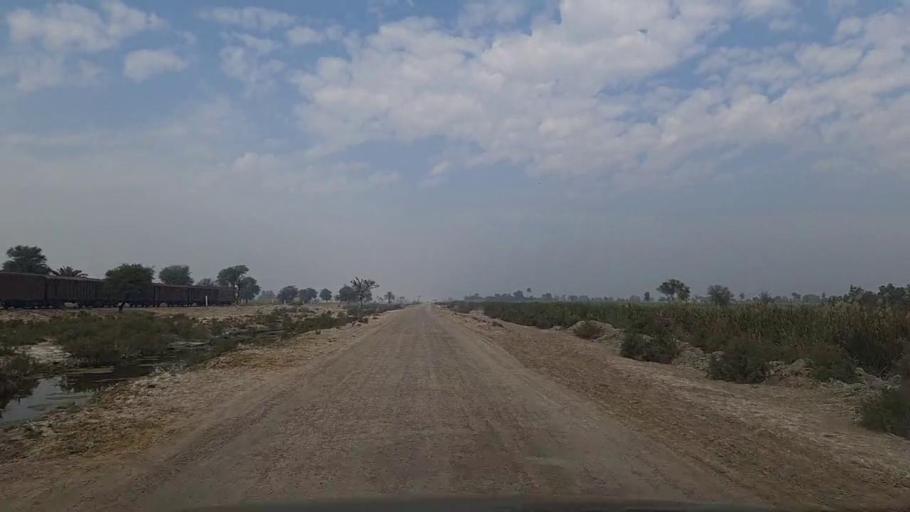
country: PK
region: Sindh
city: Daur
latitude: 26.3783
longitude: 68.3556
